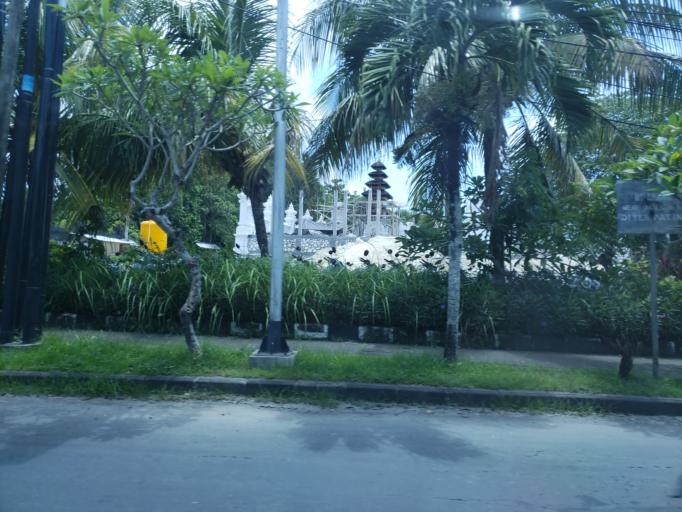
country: ID
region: Bali
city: Kangin
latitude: -8.8311
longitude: 115.1266
